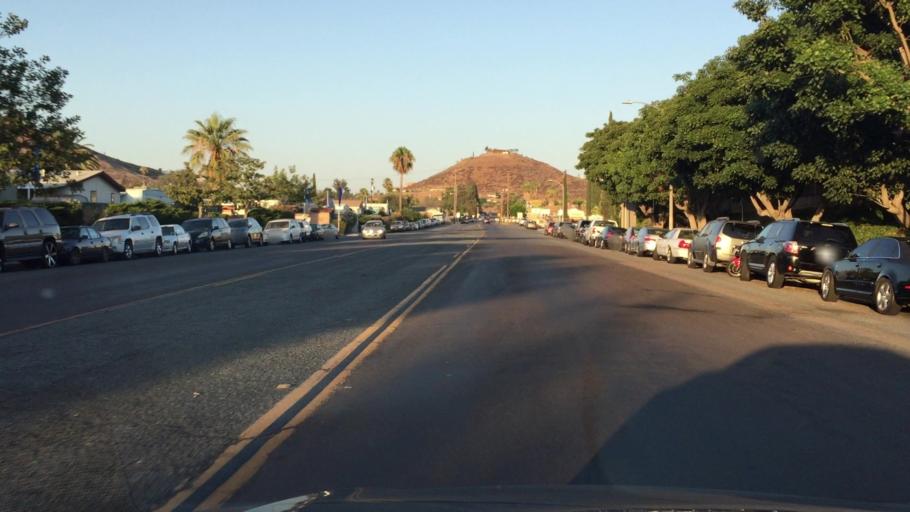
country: US
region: California
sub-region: San Diego County
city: Bostonia
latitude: 32.8191
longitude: -116.9546
